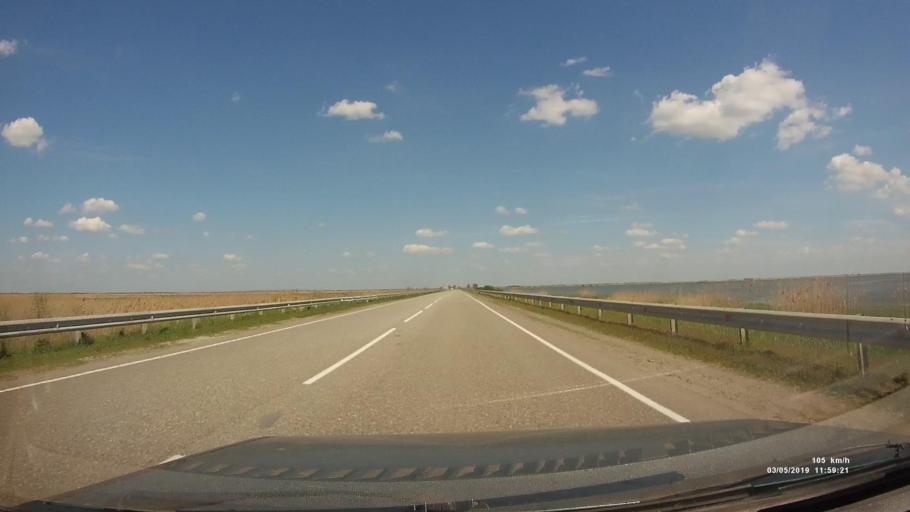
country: RU
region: Rostov
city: Bagayevskaya
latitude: 47.2335
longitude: 40.3294
